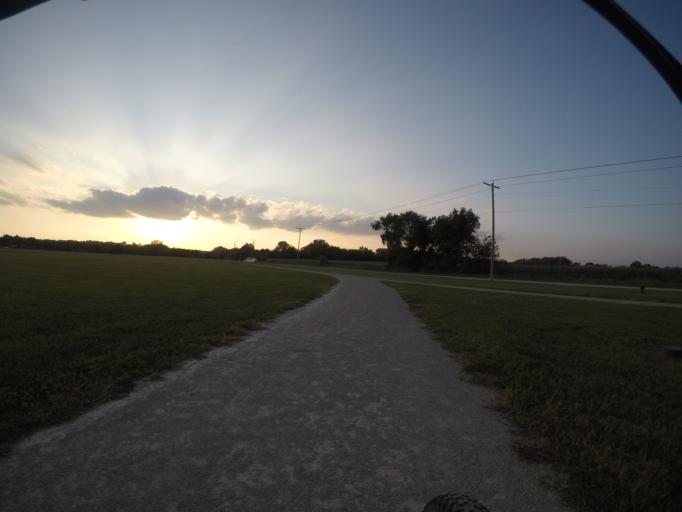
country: US
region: Kansas
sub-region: Riley County
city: Manhattan
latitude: 39.2038
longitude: -96.5455
